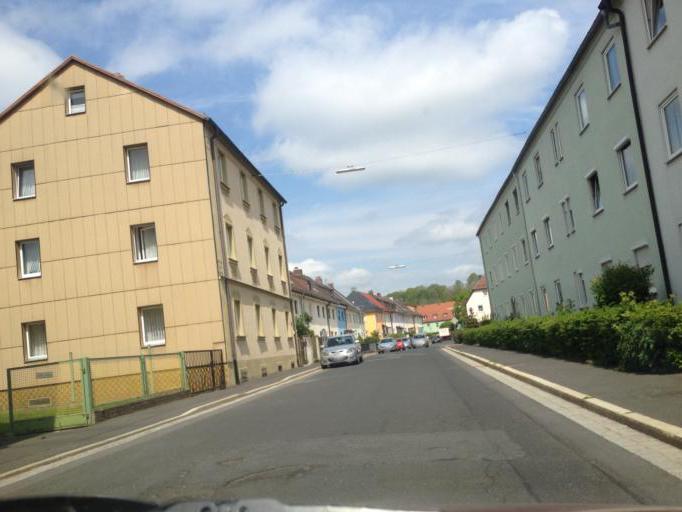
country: DE
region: Bavaria
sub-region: Upper Franconia
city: Arzberg
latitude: 50.0558
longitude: 12.1812
